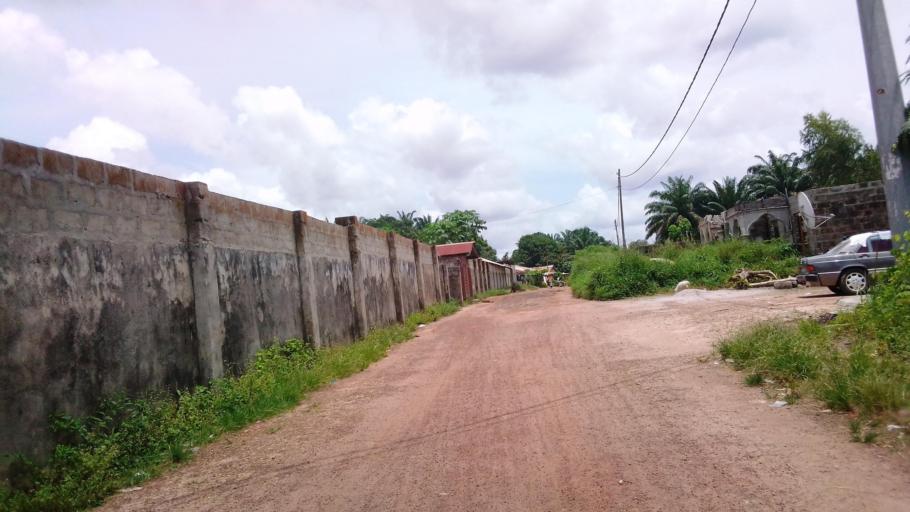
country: SL
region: Northern Province
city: Makeni
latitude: 8.8694
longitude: -12.0376
